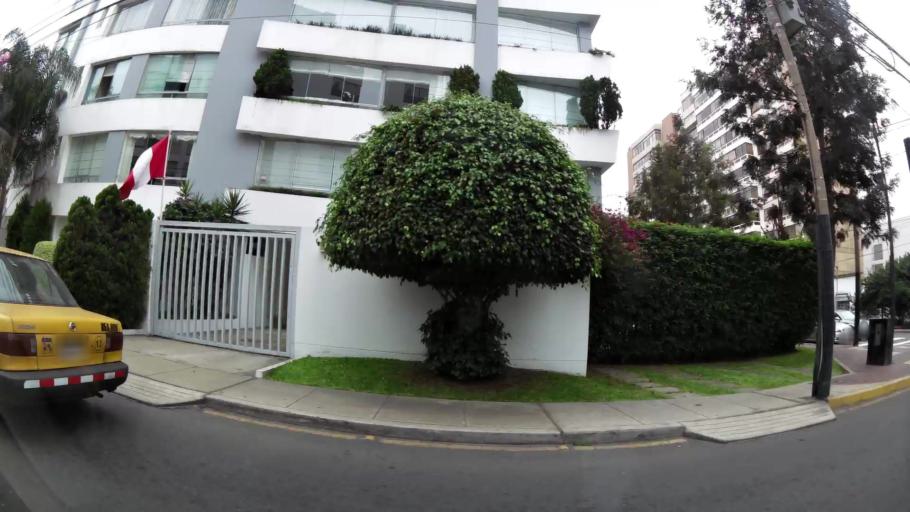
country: PE
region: Lima
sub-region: Lima
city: San Isidro
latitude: -12.0959
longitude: -77.0470
